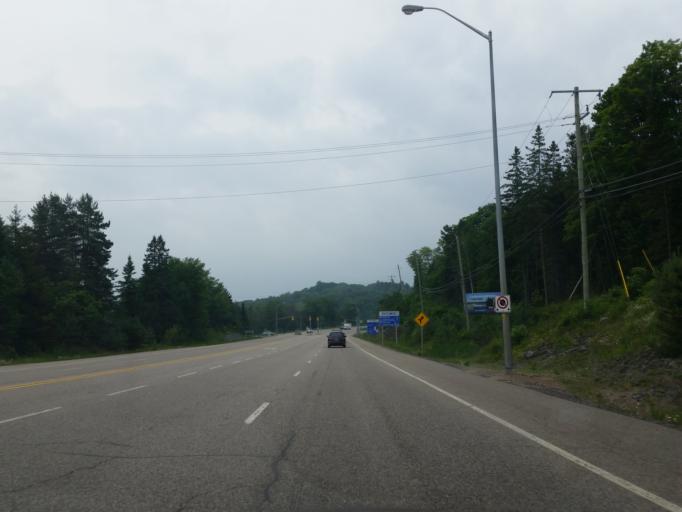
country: CA
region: Ontario
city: Huntsville
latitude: 45.3474
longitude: -79.1521
